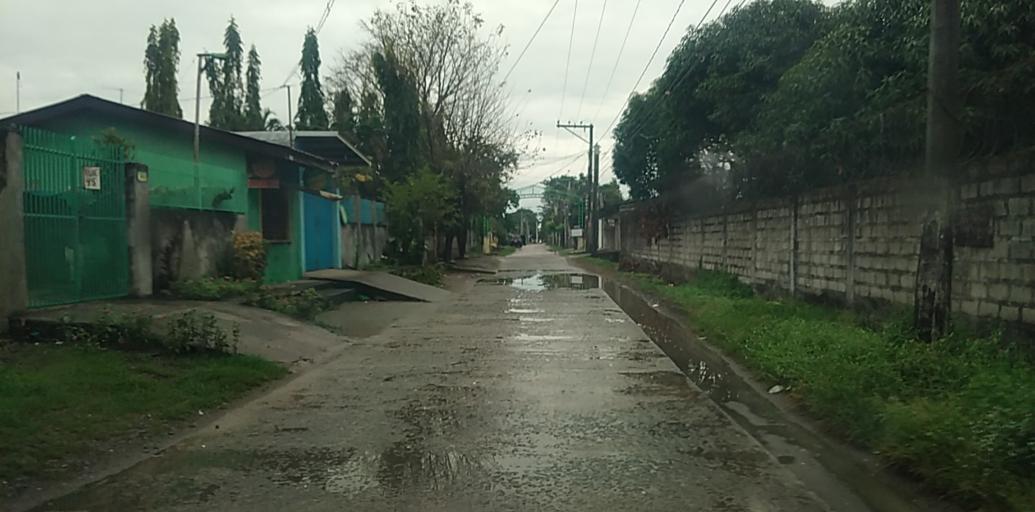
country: PH
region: Central Luzon
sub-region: Province of Pampanga
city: Arayat
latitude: 15.1482
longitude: 120.7415
